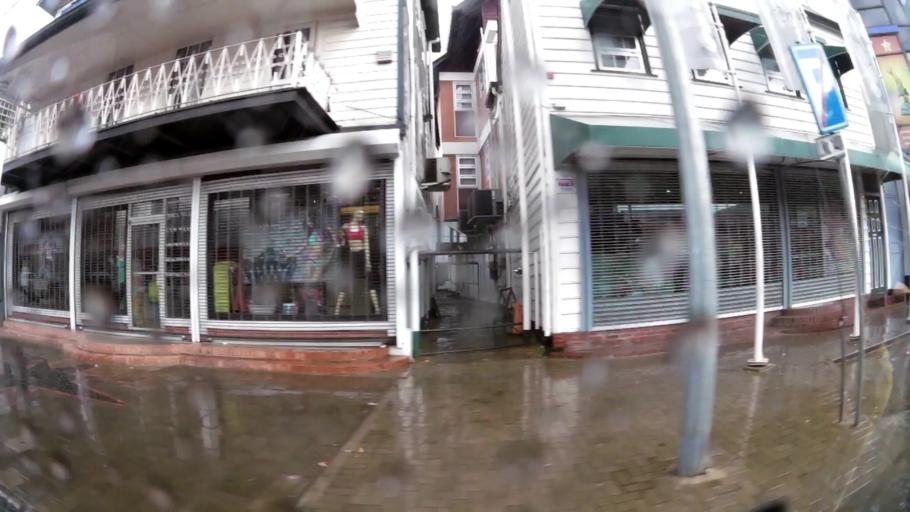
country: SR
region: Paramaribo
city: Paramaribo
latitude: 5.8283
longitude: -55.1609
